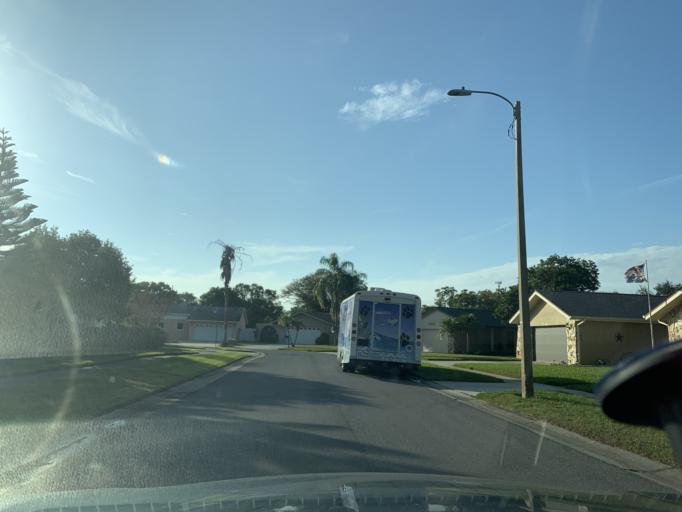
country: US
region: Florida
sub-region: Pinellas County
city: Ridgecrest
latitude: 27.8926
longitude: -82.7984
